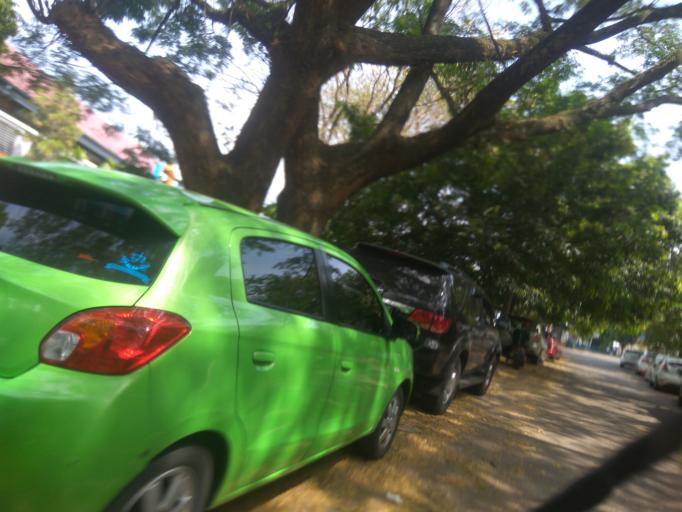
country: ID
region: Central Java
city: Semarang
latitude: -7.0519
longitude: 110.4361
